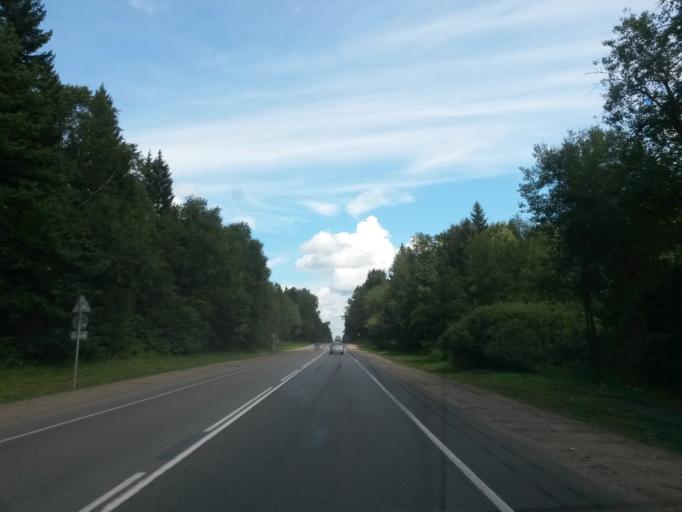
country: RU
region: Jaroslavl
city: Pereslavl'-Zalesskiy
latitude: 56.7991
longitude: 38.8925
